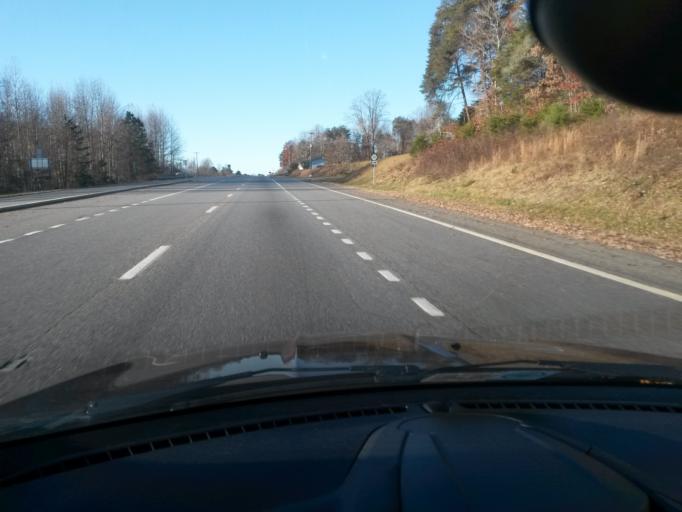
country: US
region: Virginia
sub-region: Henry County
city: Pannill Fork
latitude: 36.6020
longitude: -80.0766
